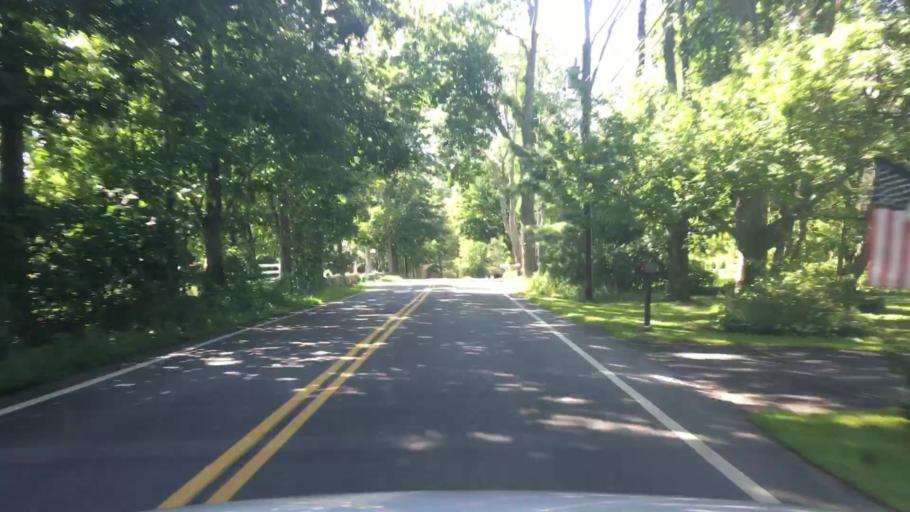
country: US
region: New Hampshire
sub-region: Strafford County
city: Dover
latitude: 43.1816
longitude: -70.8406
